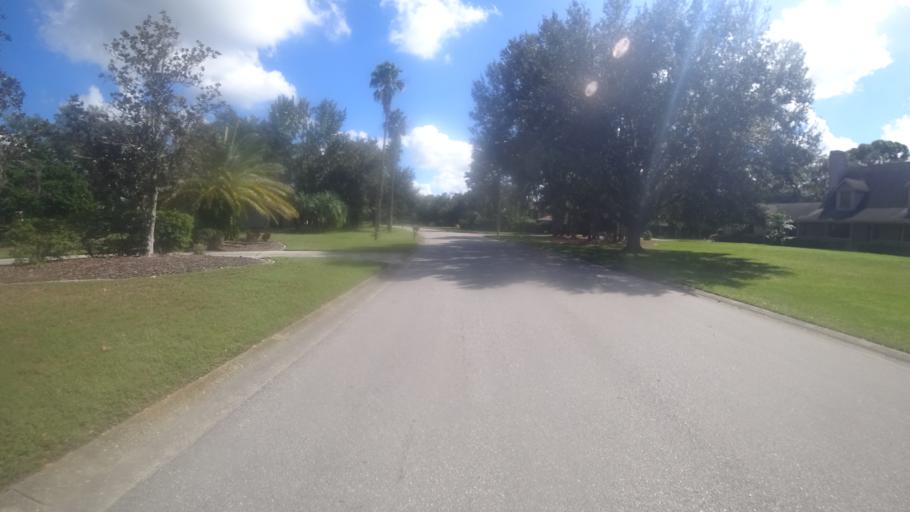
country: US
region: Florida
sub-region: Manatee County
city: Ellenton
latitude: 27.4959
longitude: -82.4044
